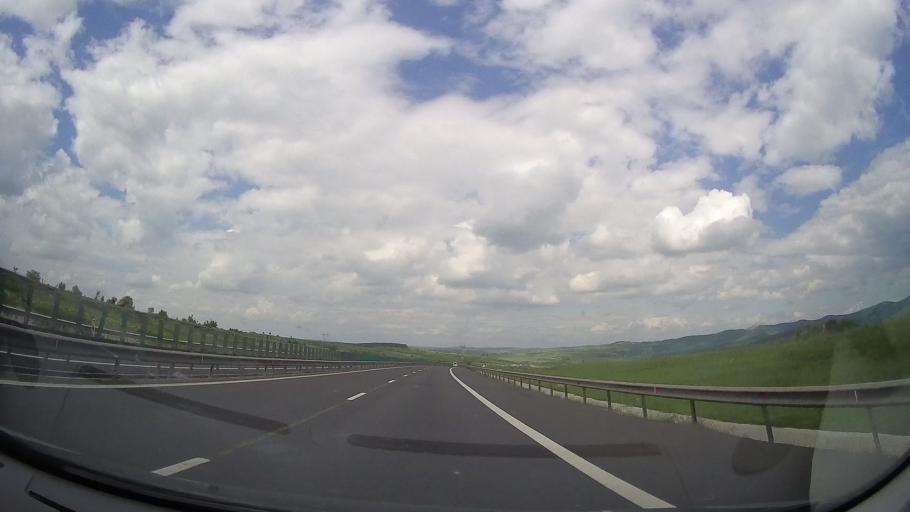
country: RO
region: Sibiu
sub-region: Comuna Apoldu de Jos
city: Apoldu de Jos
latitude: 45.8387
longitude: 23.8634
